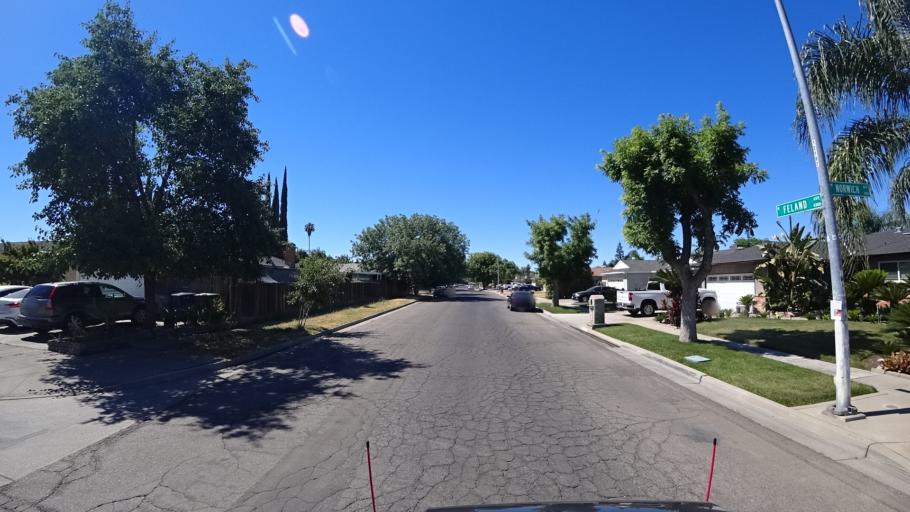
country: US
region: California
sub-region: Fresno County
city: West Park
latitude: 36.8002
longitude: -119.8484
